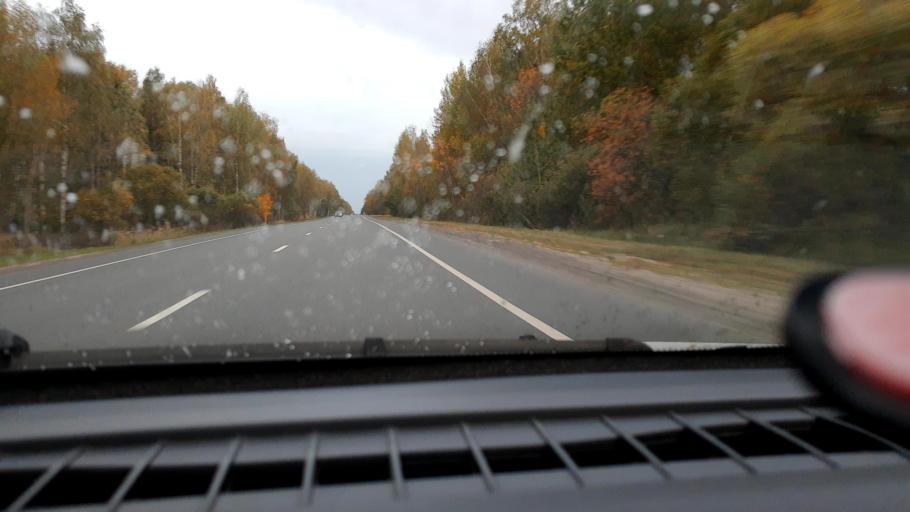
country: RU
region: Vladimir
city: Orgtrud
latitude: 56.2047
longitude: 40.7312
